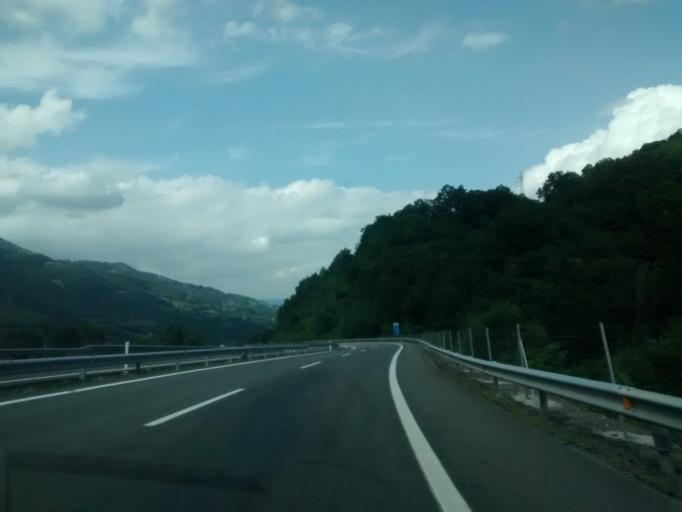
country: ES
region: Asturias
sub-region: Province of Asturias
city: Pola de Lena
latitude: 43.0784
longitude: -5.8261
